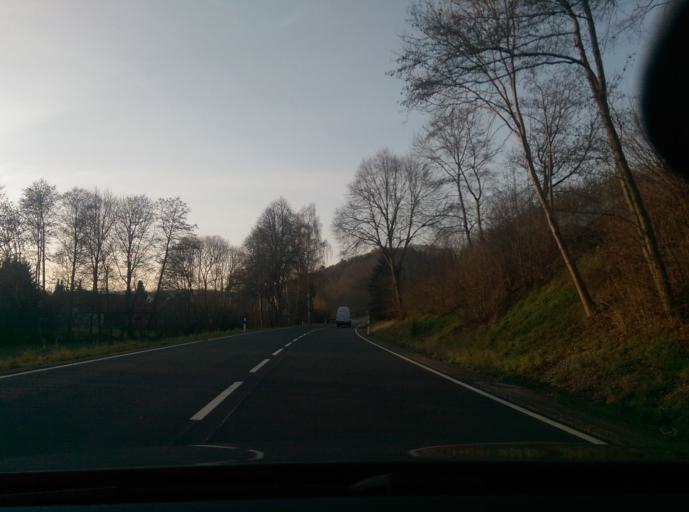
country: DE
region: Thuringia
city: Lauchroden
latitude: 51.0228
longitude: 10.1009
